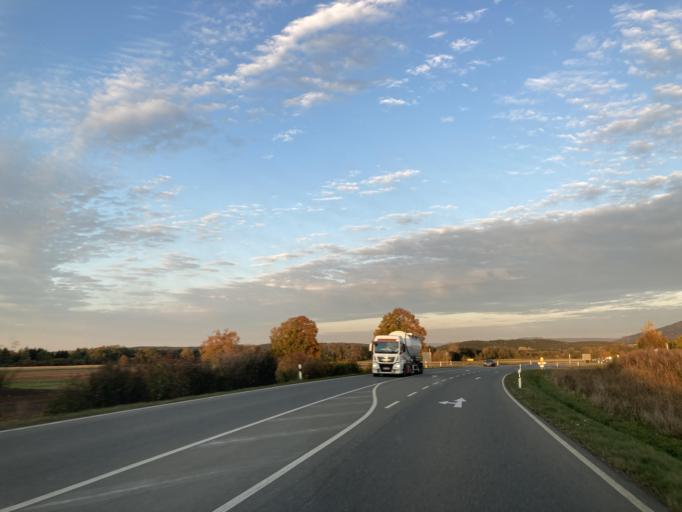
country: DE
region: Baden-Wuerttemberg
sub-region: Tuebingen Region
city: Zimmern unter der Burg
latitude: 48.1992
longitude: 8.7030
